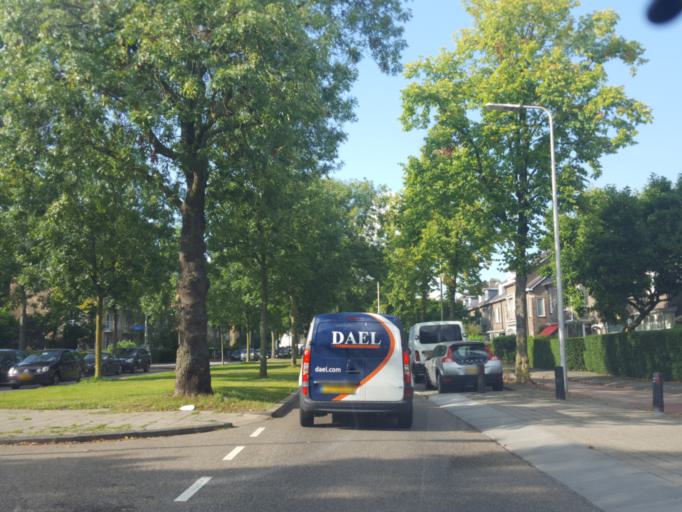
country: NL
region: Utrecht
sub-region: Gemeente Utrecht
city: Utrecht
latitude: 52.0886
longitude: 5.0830
